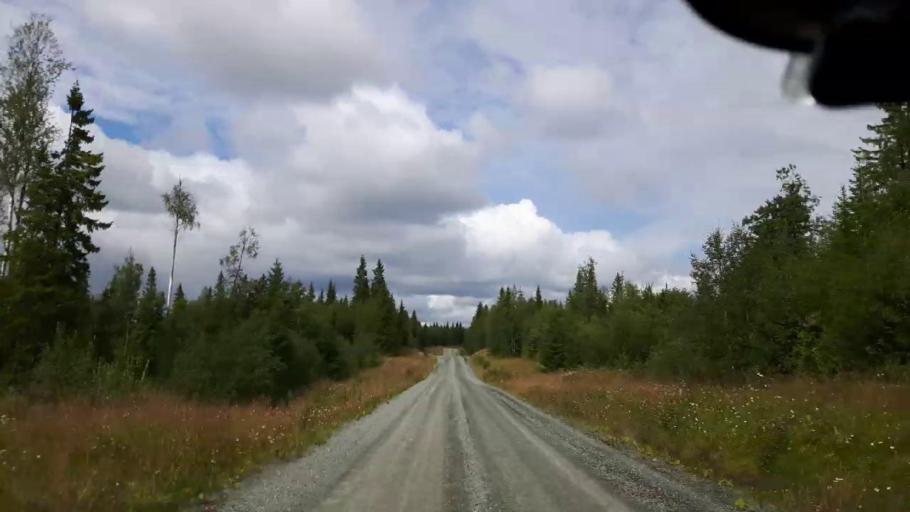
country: SE
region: Jaemtland
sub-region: Krokoms Kommun
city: Valla
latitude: 63.5575
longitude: 13.9171
